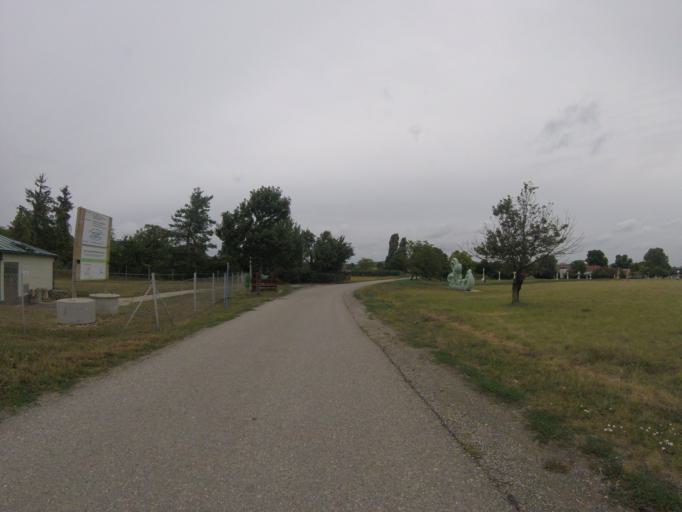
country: AT
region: Burgenland
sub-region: Politischer Bezirk Neusiedl am See
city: Winden am See
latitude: 47.9586
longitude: 16.7443
